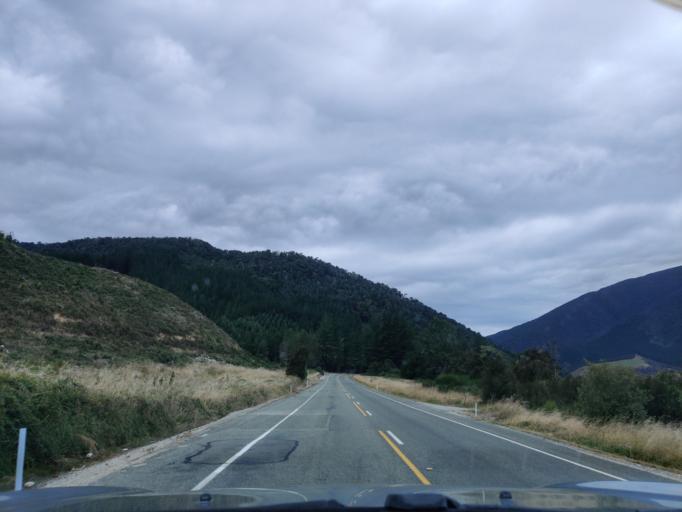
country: NZ
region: Tasman
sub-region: Tasman District
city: Wakefield
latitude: -41.6883
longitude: 172.4634
